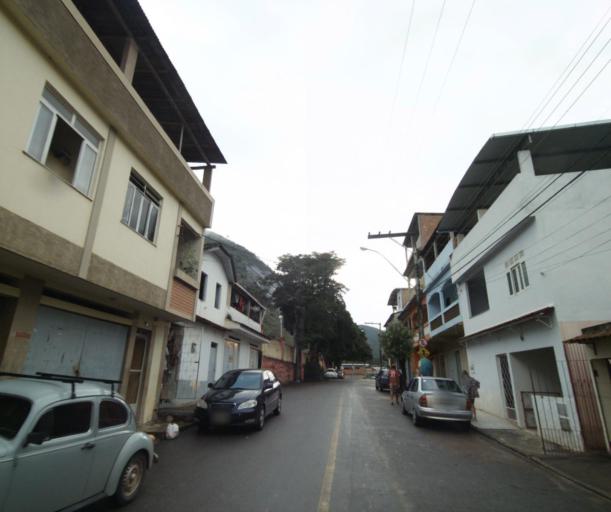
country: BR
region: Espirito Santo
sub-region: Muniz Freire
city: Muniz Freire
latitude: -20.4627
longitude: -41.4188
